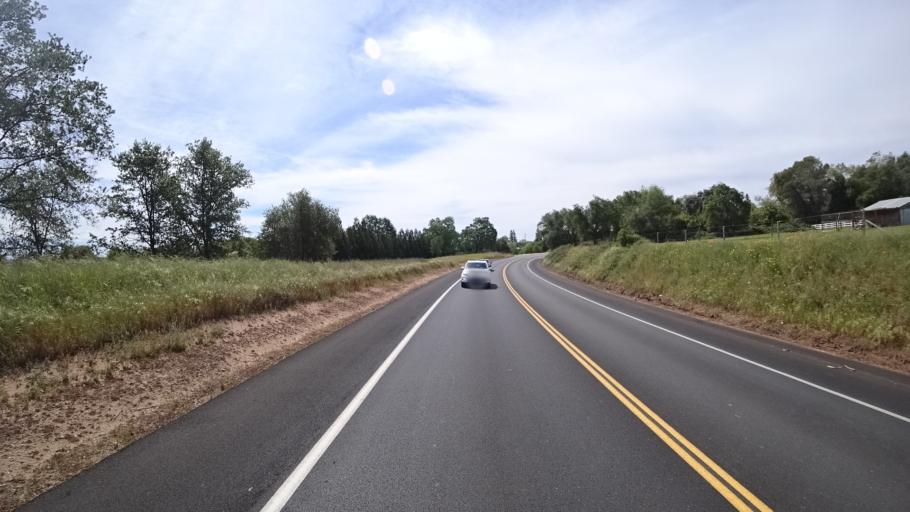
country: US
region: California
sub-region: Placer County
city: Loomis
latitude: 38.8334
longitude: -121.2183
